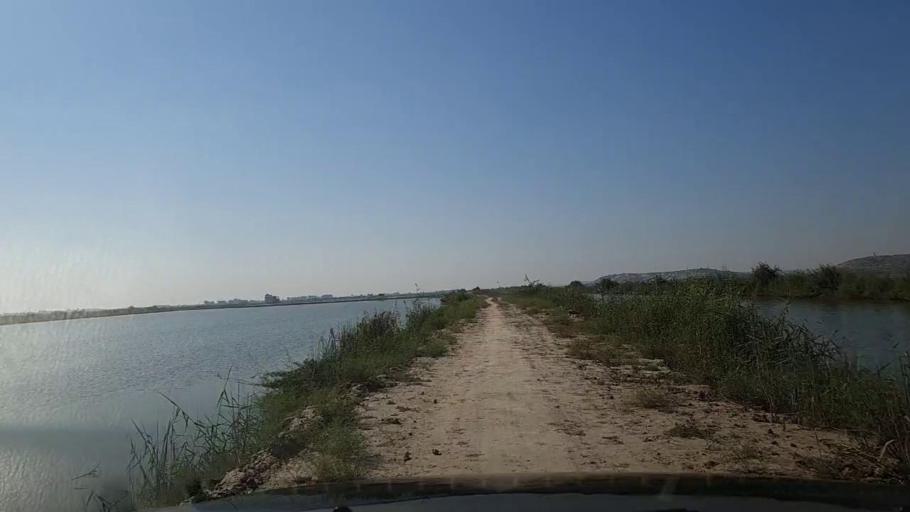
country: PK
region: Sindh
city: Thatta
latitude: 24.6884
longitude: 67.8931
